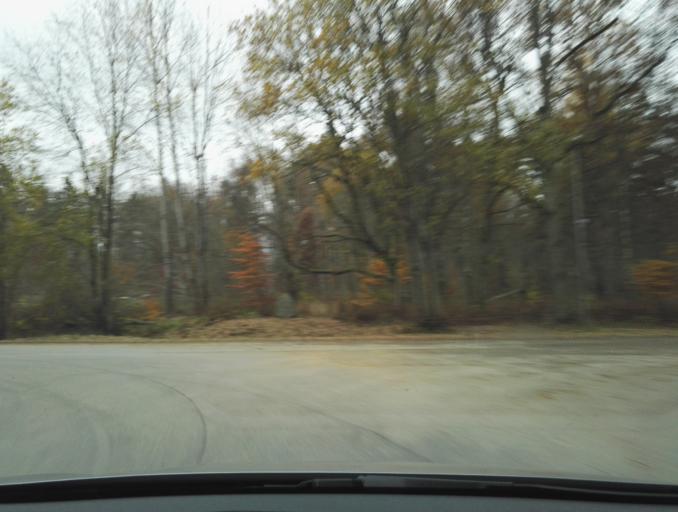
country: SE
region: Kronoberg
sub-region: Vaxjo Kommun
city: Vaexjoe
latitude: 56.8753
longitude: 14.7764
